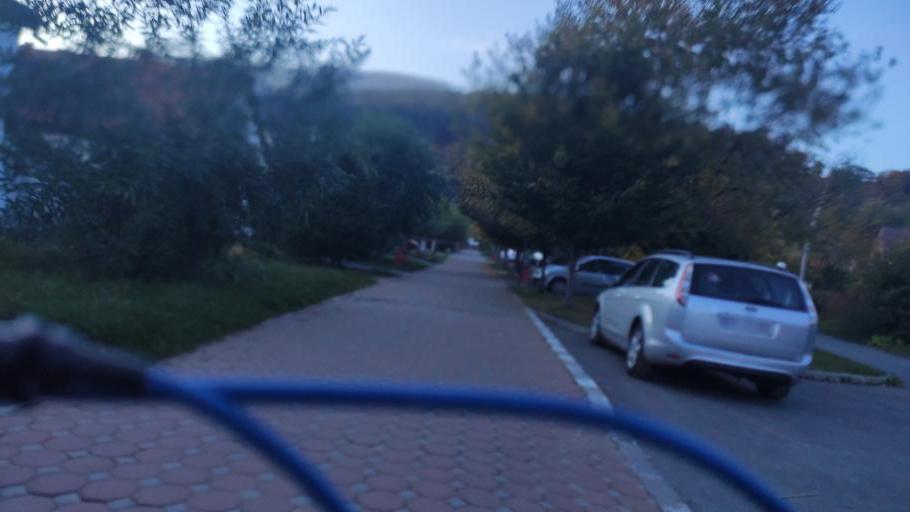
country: RO
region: Brasov
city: Codlea
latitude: 45.7006
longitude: 25.4407
